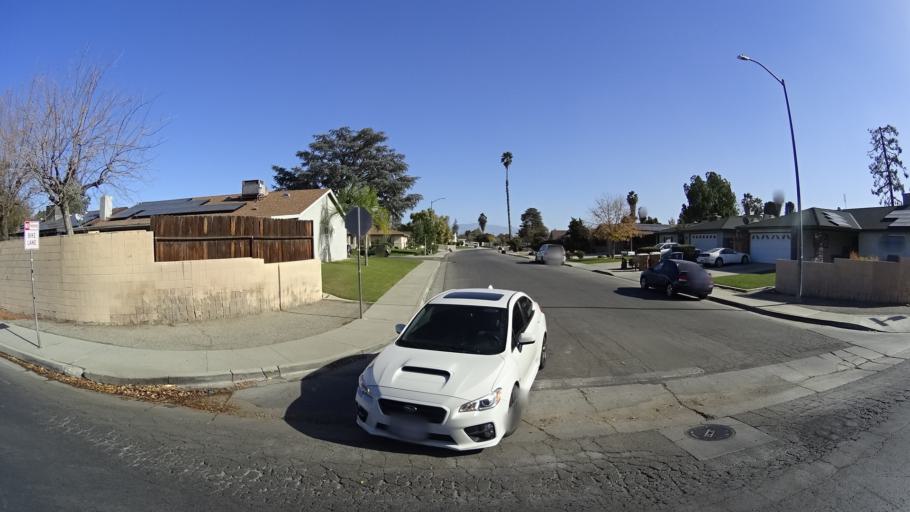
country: US
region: California
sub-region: Kern County
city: Bakersfield
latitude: 35.3356
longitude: -119.0596
